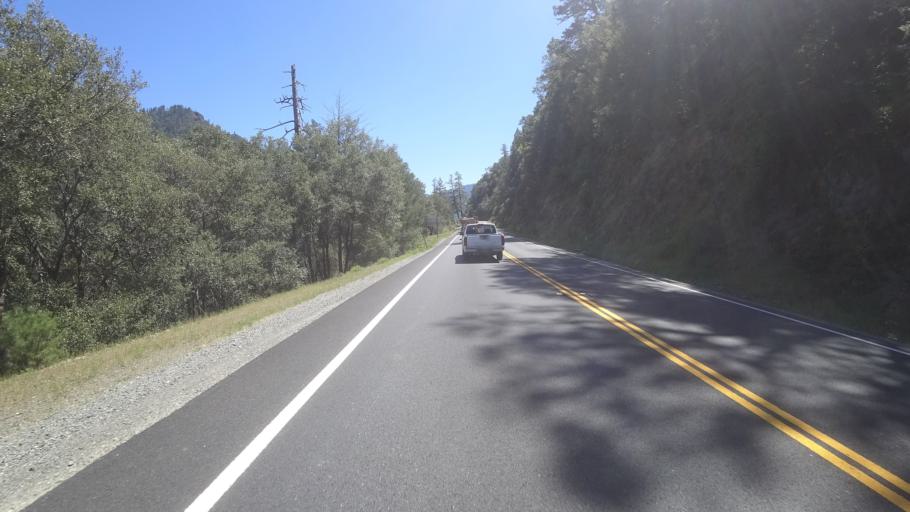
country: US
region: California
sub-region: Humboldt County
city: Willow Creek
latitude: 40.8201
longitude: -123.4814
